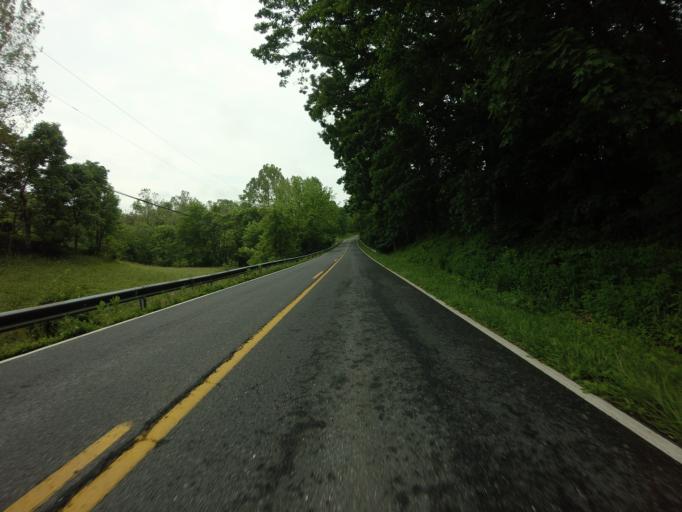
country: US
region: Maryland
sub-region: Frederick County
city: Jefferson
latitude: 39.3314
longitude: -77.5514
